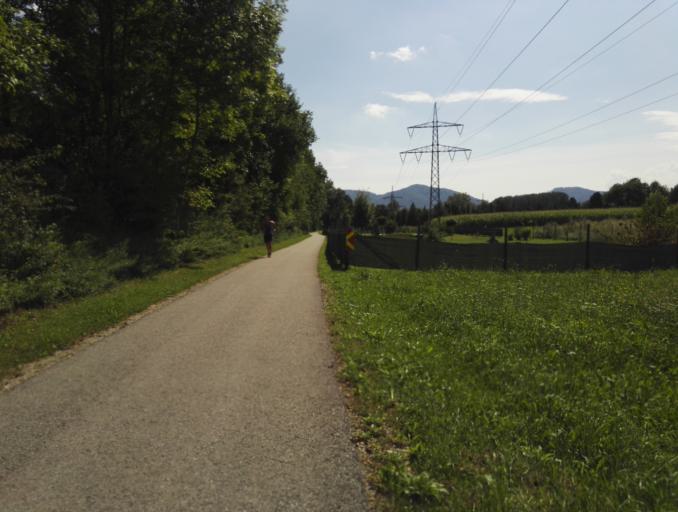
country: AT
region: Styria
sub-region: Politischer Bezirk Graz-Umgebung
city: Gratkorn
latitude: 47.1425
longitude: 15.3280
